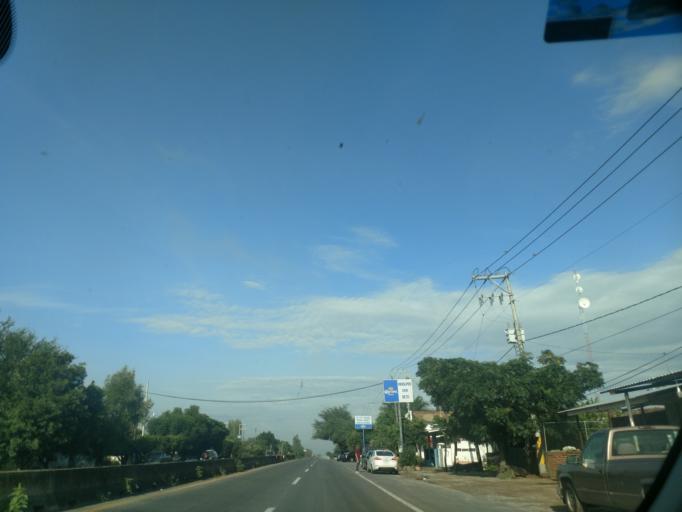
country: MX
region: Jalisco
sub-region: Ameca
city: Los Pocitos
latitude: 20.5369
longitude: -103.9384
